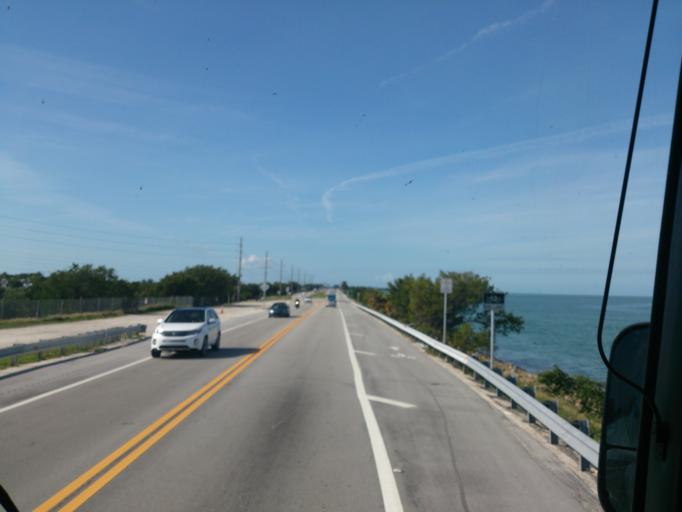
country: US
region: Florida
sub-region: Monroe County
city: Marathon
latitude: 24.7820
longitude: -80.9099
